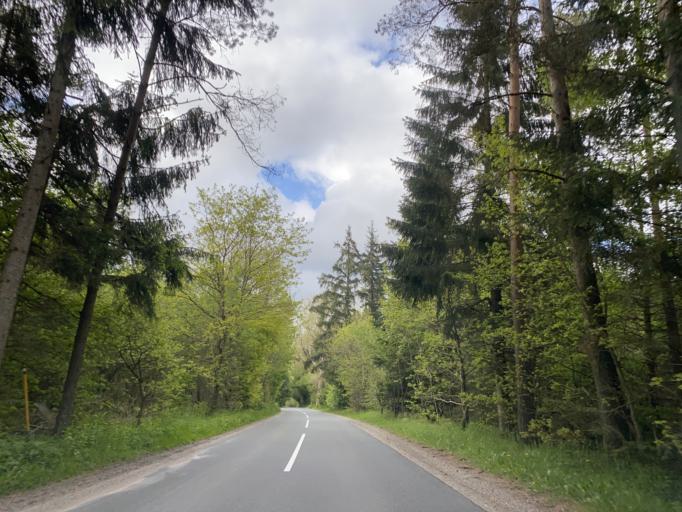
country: DK
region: Central Jutland
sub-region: Horsens Kommune
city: Braedstrup
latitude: 56.0305
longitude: 9.6553
